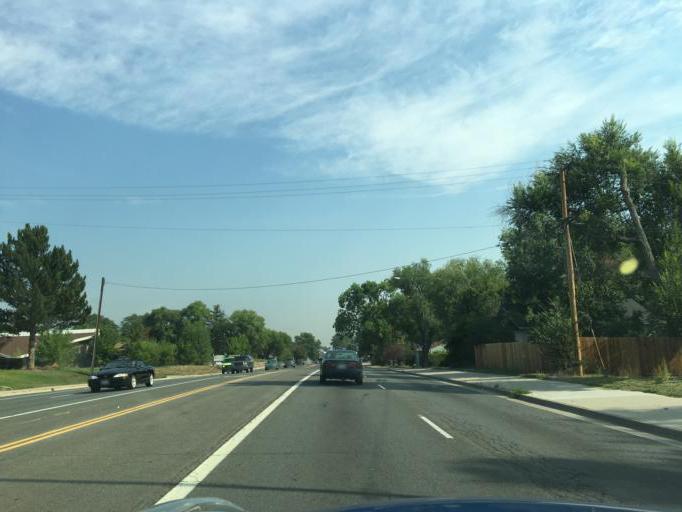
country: US
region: Colorado
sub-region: Jefferson County
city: Wheat Ridge
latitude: 39.7499
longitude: -105.0814
